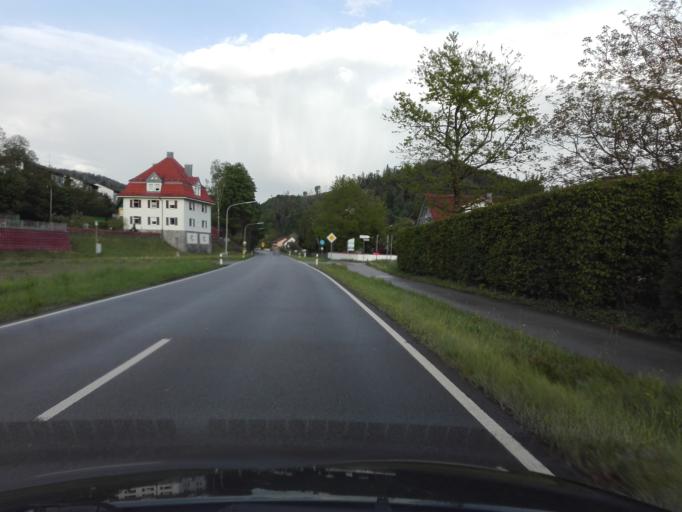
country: DE
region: Bavaria
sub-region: Lower Bavaria
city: Obernzell
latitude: 48.5624
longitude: 13.5737
